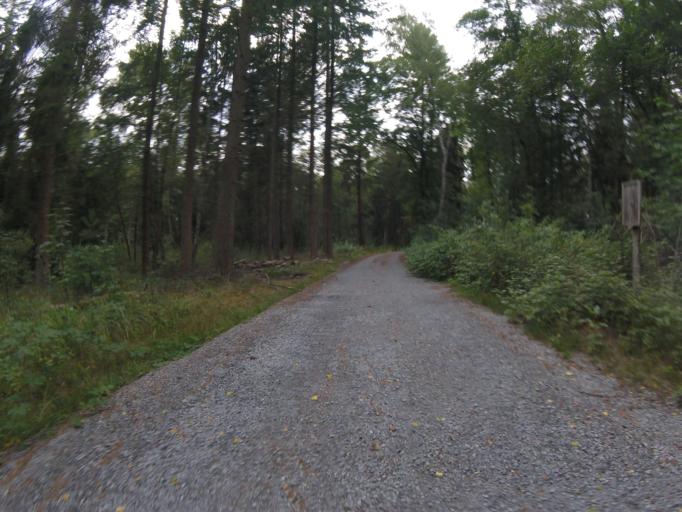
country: DE
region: Brandenburg
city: Halbe
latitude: 52.1521
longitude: 13.7466
